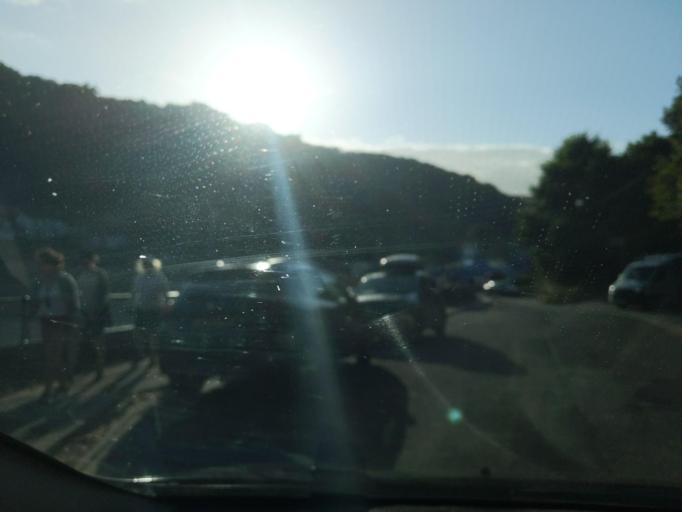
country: GB
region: England
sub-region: Devon
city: Salcombe
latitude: 50.2301
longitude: -3.7797
